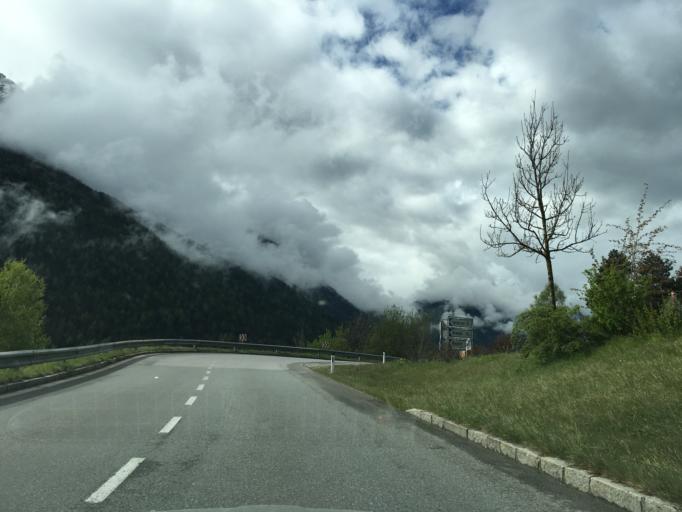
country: AT
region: Tyrol
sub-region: Politischer Bezirk Innsbruck Land
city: Fulpmes
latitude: 47.1585
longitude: 11.3552
